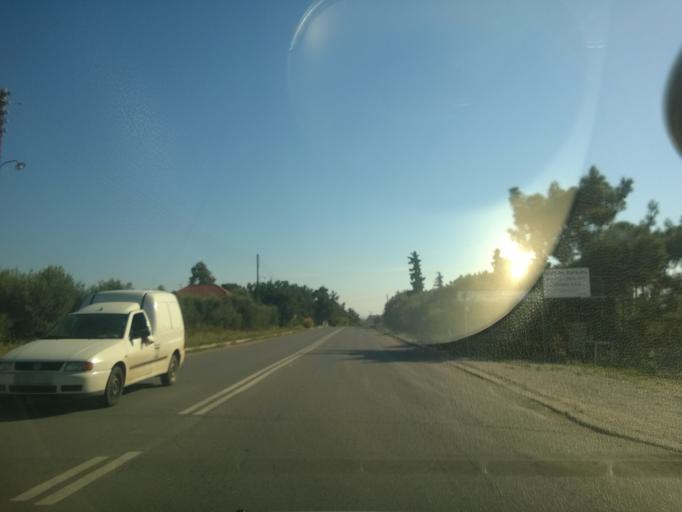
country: GR
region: Central Macedonia
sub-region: Nomos Chalkidikis
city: Nea Kallikrateia
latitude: 40.3463
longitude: 23.0604
